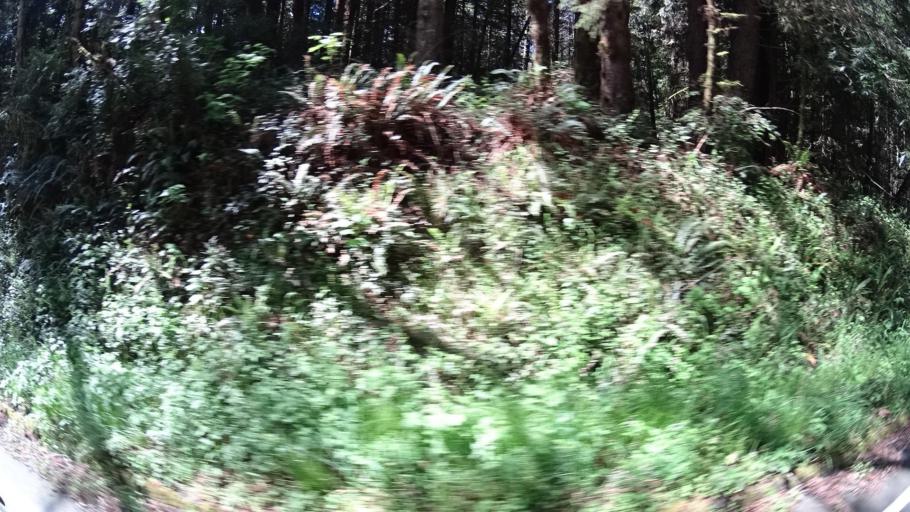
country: US
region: California
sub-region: Humboldt County
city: McKinleyville
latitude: 40.9712
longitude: -124.0616
